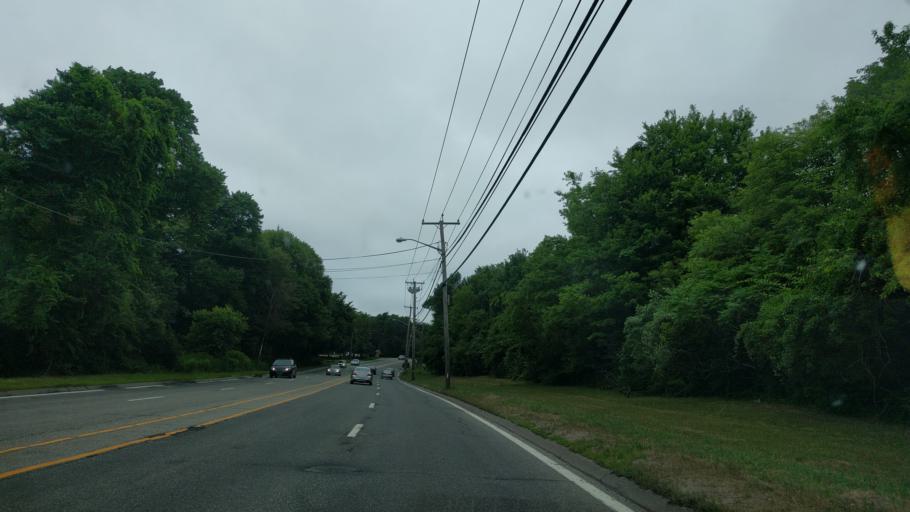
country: US
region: Rhode Island
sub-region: Newport County
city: Middletown
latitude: 41.5609
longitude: -71.2867
